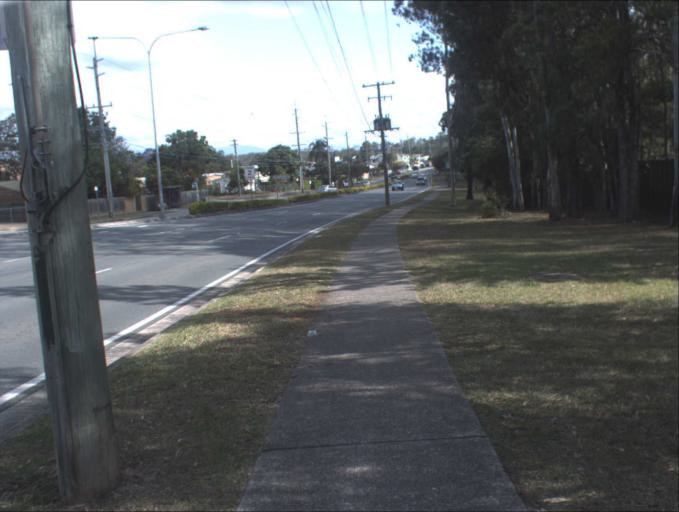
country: AU
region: Queensland
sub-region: Logan
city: Logan City
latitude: -27.6509
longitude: 153.1183
